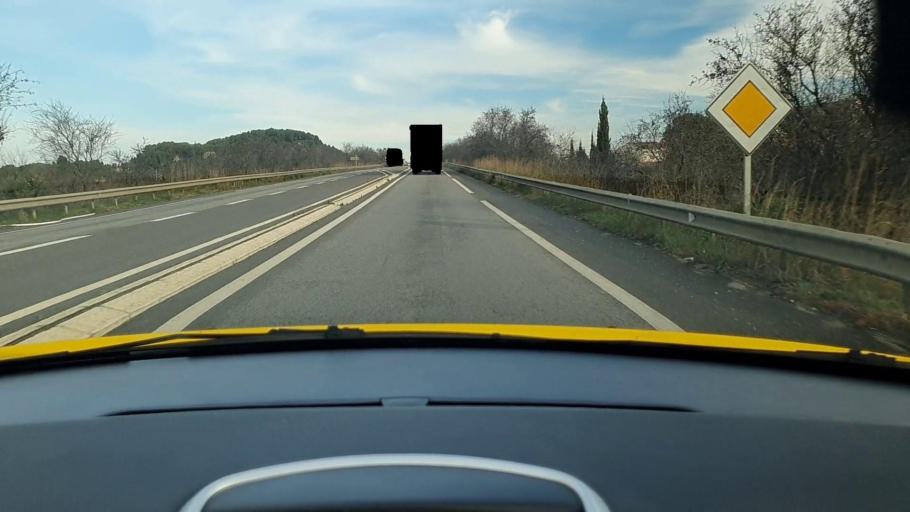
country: FR
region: Languedoc-Roussillon
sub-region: Departement du Gard
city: Beaucaire
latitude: 43.8030
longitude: 4.6085
